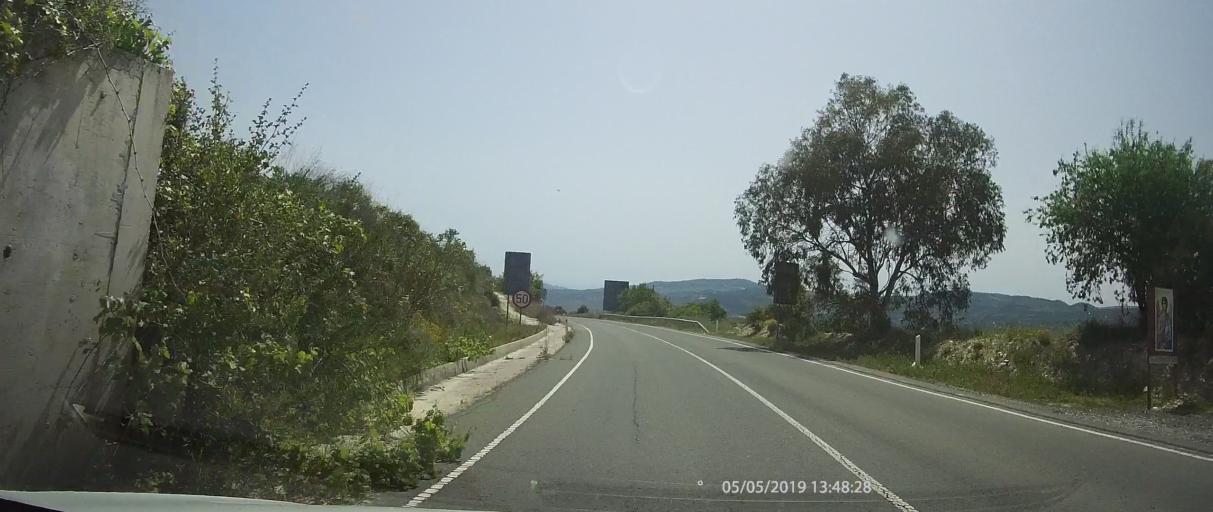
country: CY
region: Limassol
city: Pachna
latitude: 34.8576
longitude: 32.7531
